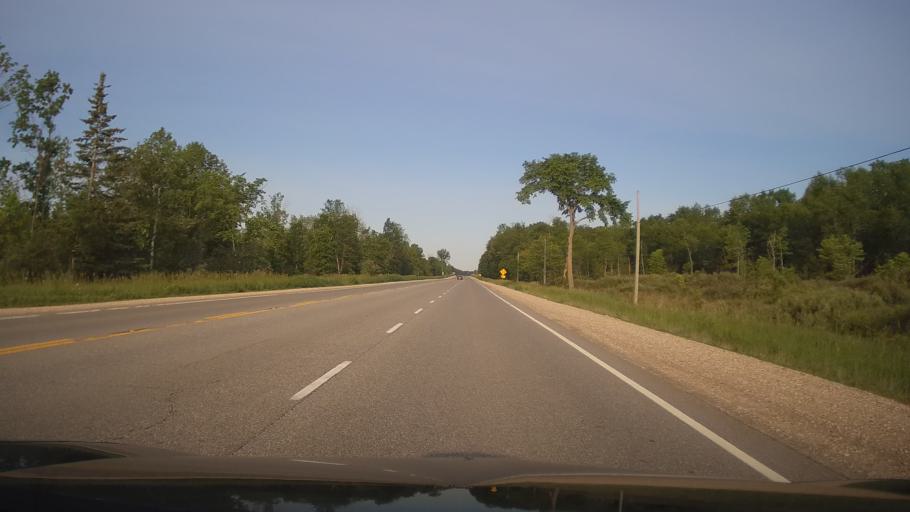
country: CA
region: Ontario
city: Perth
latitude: 44.8743
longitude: -76.3606
